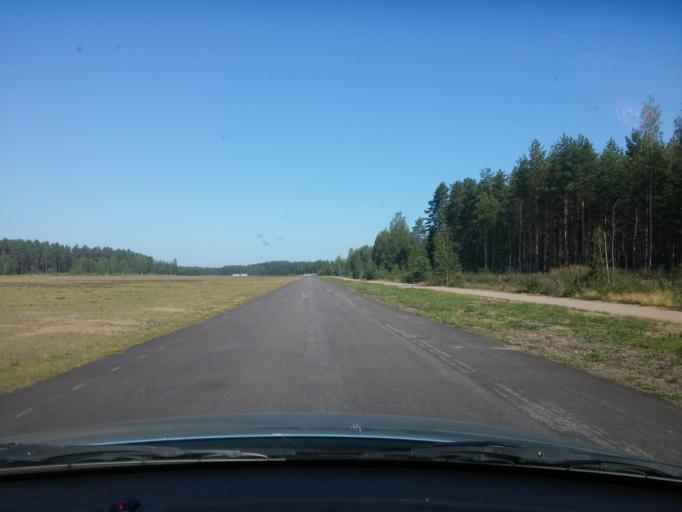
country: FI
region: Uusimaa
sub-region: Helsinki
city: Kaerkoelae
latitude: 60.7481
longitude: 24.1069
